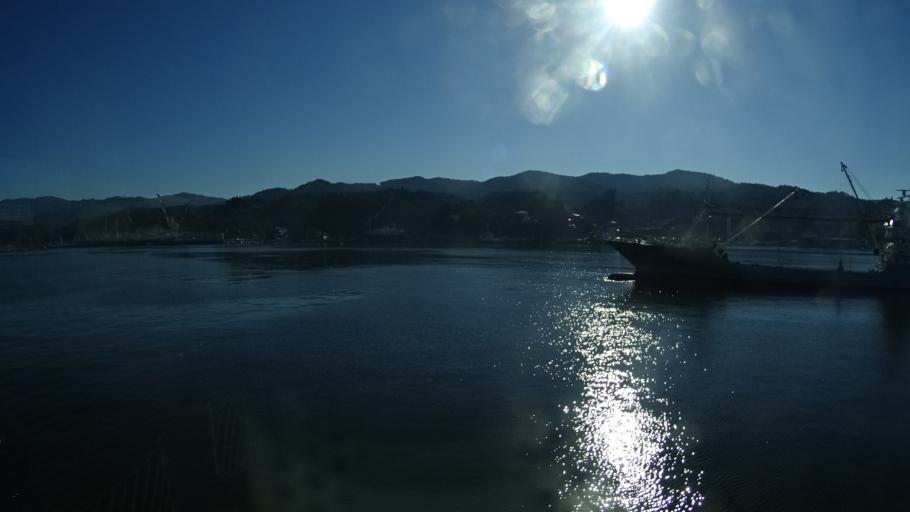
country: JP
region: Iwate
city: Ofunato
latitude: 38.9025
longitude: 141.5829
